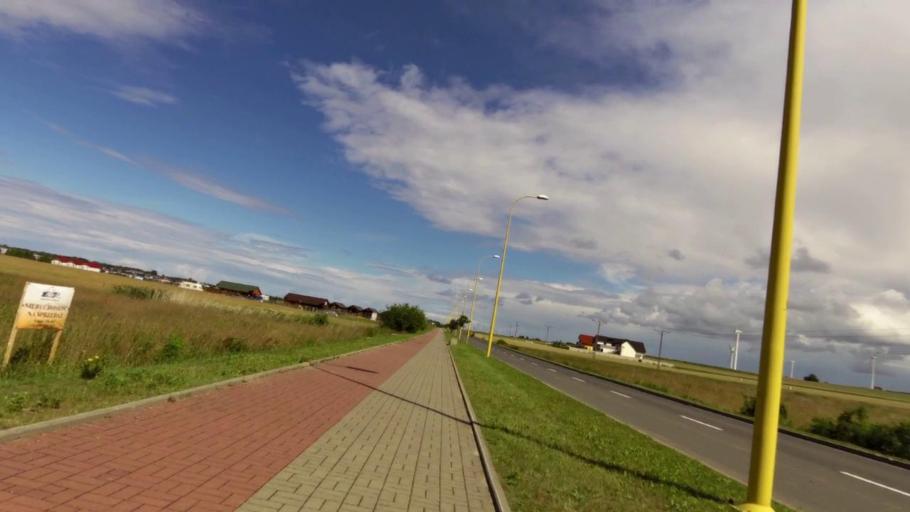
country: PL
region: West Pomeranian Voivodeship
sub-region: Powiat slawienski
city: Darlowo
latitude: 54.4354
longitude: 16.4103
